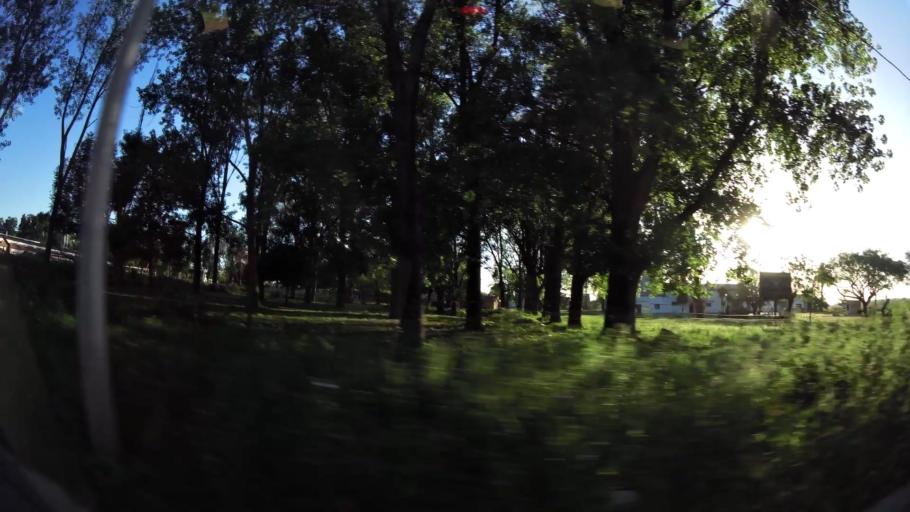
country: UY
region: Montevideo
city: Montevideo
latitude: -34.8451
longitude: -56.1810
